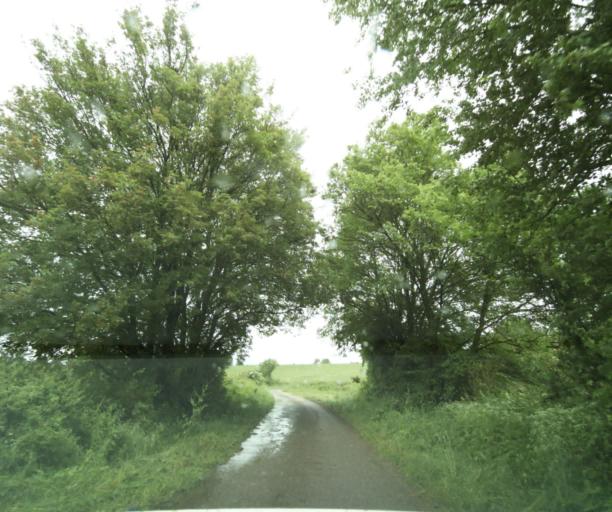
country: FR
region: Bourgogne
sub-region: Departement de Saone-et-Loire
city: Charolles
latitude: 46.5025
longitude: 4.3560
